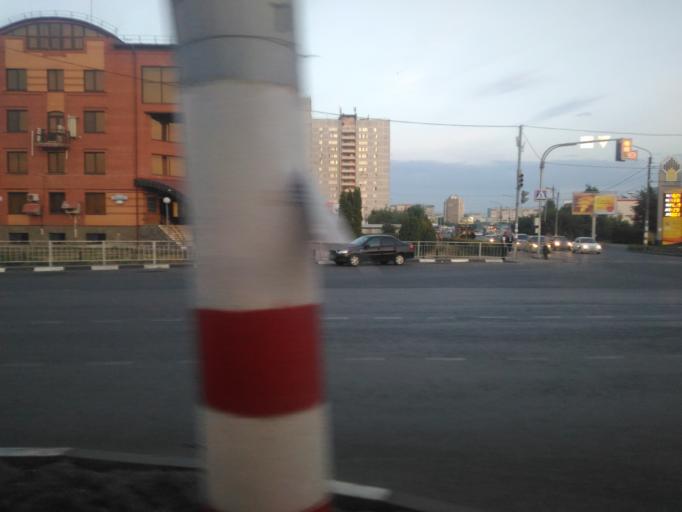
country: RU
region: Ulyanovsk
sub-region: Ulyanovskiy Rayon
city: Ulyanovsk
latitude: 54.2853
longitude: 48.3023
